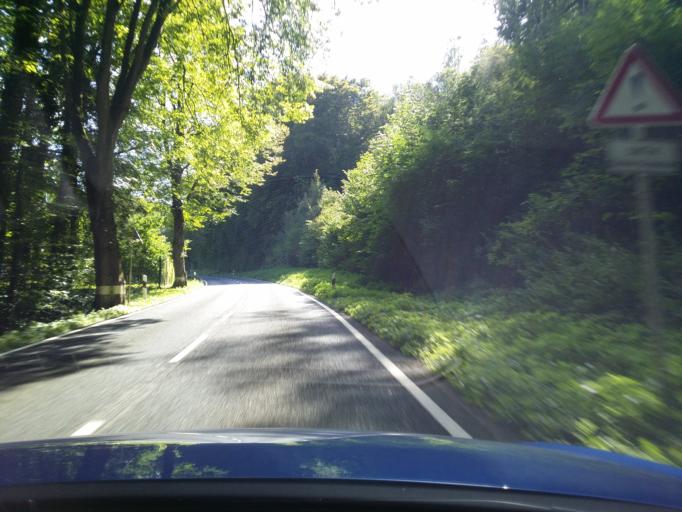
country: LU
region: Luxembourg
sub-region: Canton de Luxembourg
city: Bertrange
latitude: 49.6271
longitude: 6.0420
